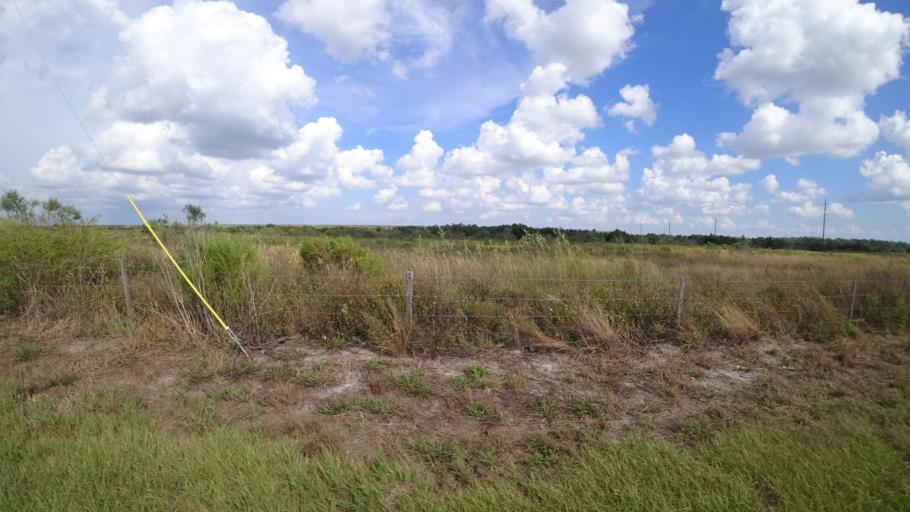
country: US
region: Florida
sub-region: Hardee County
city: Wauchula
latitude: 27.5329
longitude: -82.0778
